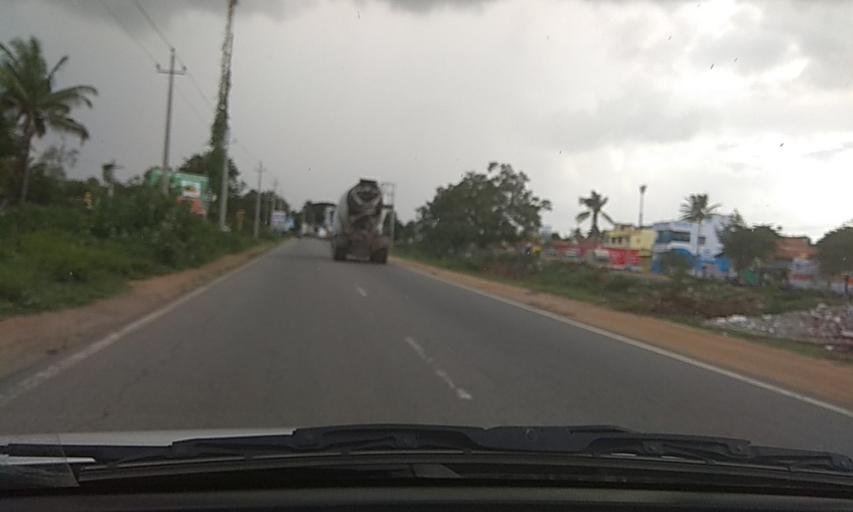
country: IN
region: Karnataka
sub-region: Mandya
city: Shrirangapattana
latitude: 12.3822
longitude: 76.6672
